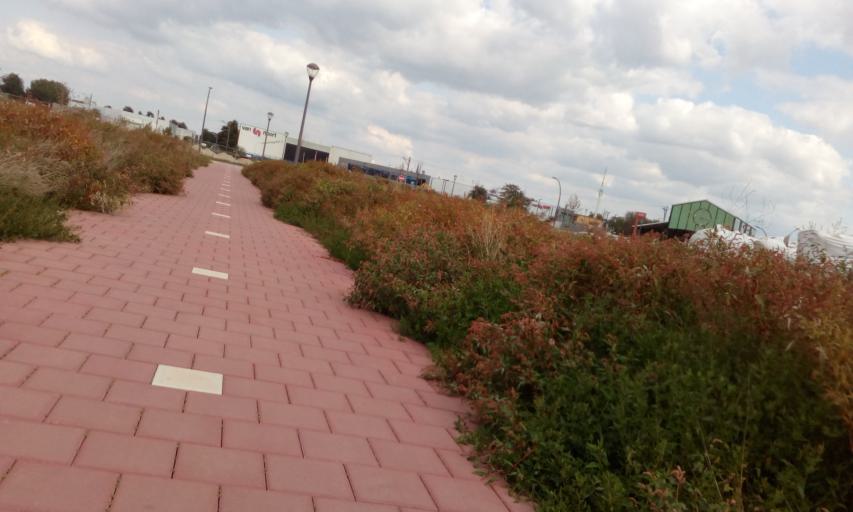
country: NL
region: South Holland
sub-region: Gemeente Waddinxveen
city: Waddinxveen
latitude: 52.0268
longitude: 4.6468
